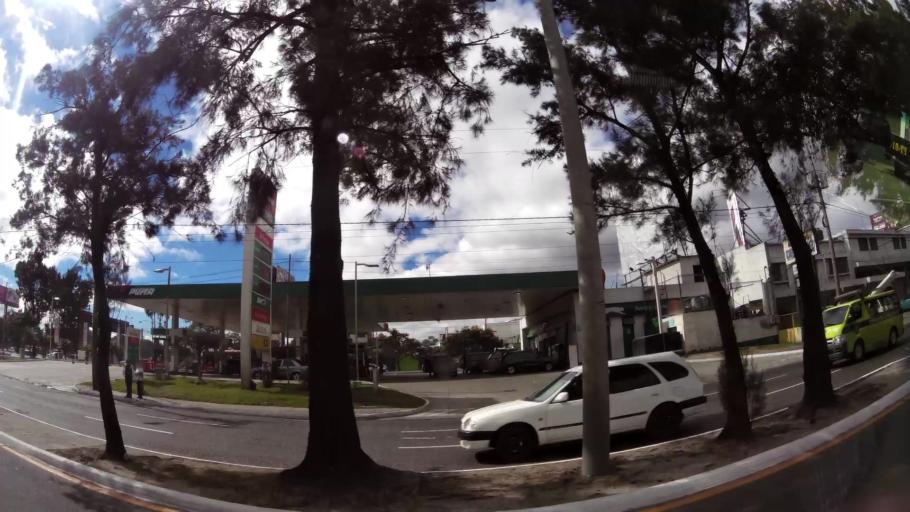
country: GT
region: Guatemala
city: Guatemala City
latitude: 14.6188
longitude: -90.5424
